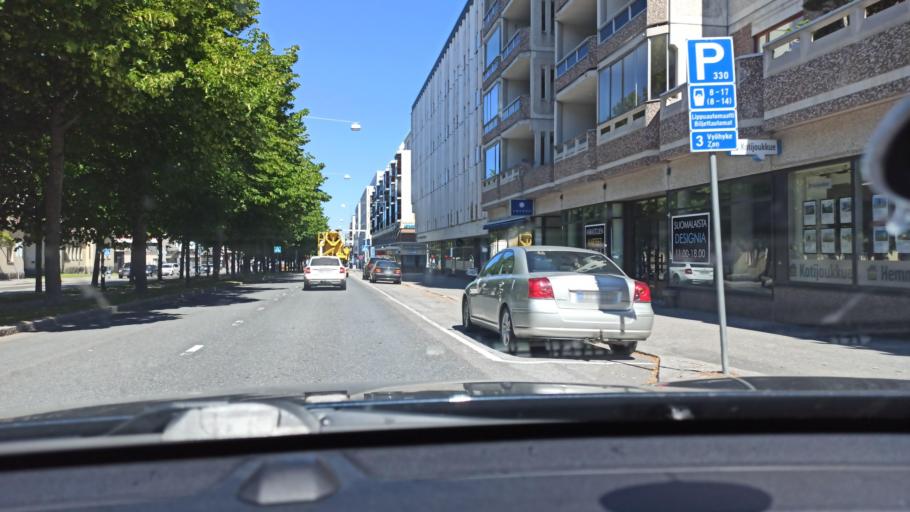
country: FI
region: Ostrobothnia
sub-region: Vaasa
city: Vaasa
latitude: 63.0923
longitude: 21.6192
